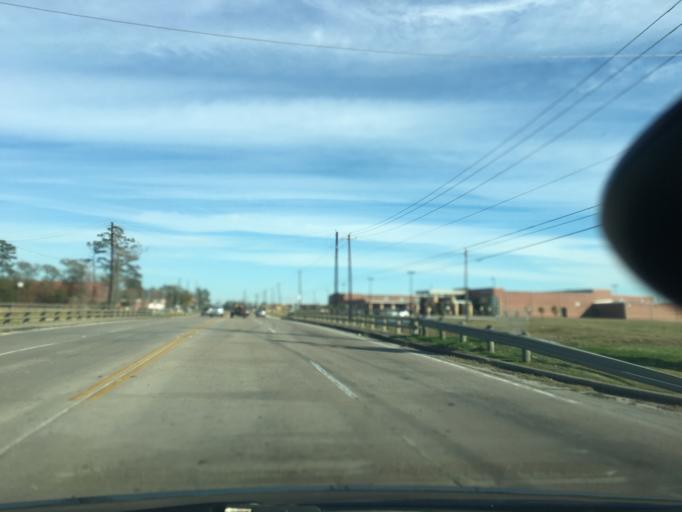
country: US
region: Texas
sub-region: Harris County
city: Cloverleaf
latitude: 29.8098
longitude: -95.1592
